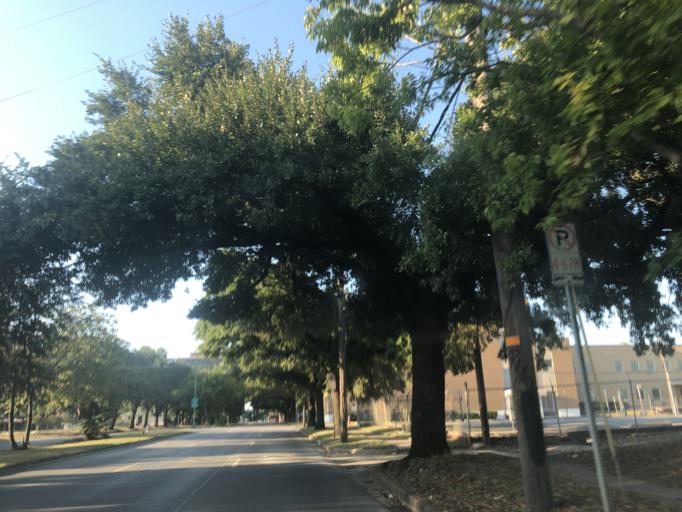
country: US
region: Texas
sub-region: Dallas County
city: Dallas
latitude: 32.7470
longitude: -96.8247
